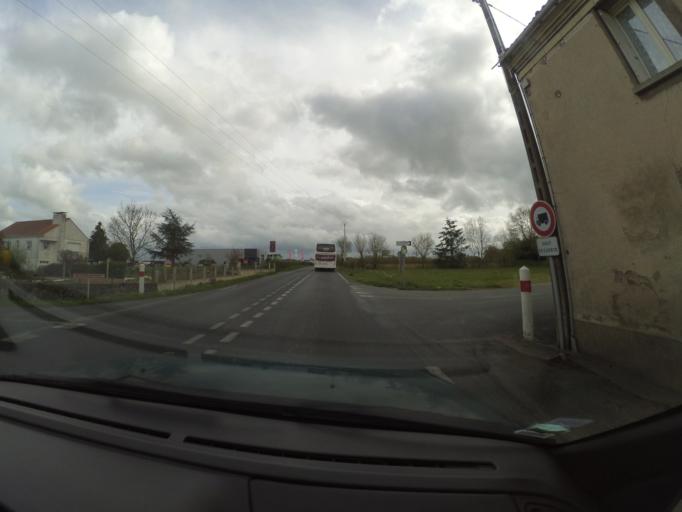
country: FR
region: Pays de la Loire
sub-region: Departement de Maine-et-Loire
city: Lire
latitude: 47.3264
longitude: -1.1666
